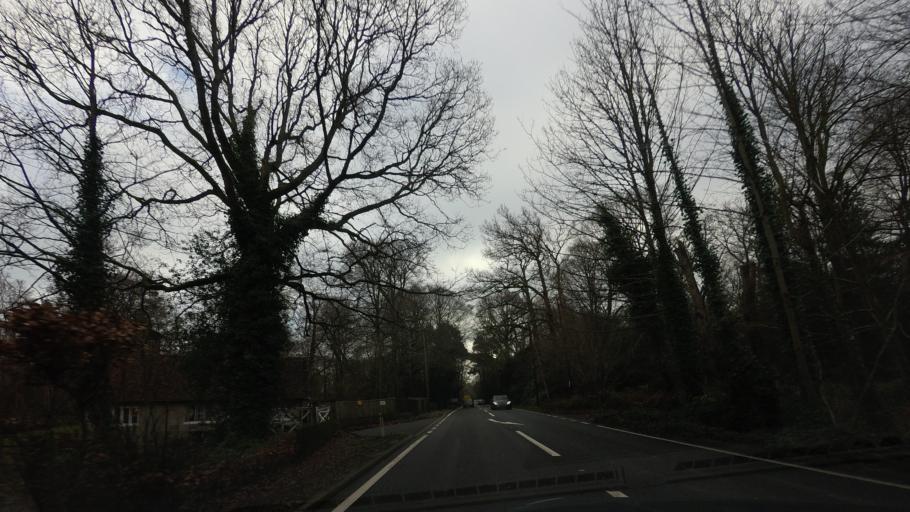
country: GB
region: England
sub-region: East Sussex
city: Wadhurst
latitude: 51.0834
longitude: 0.4145
